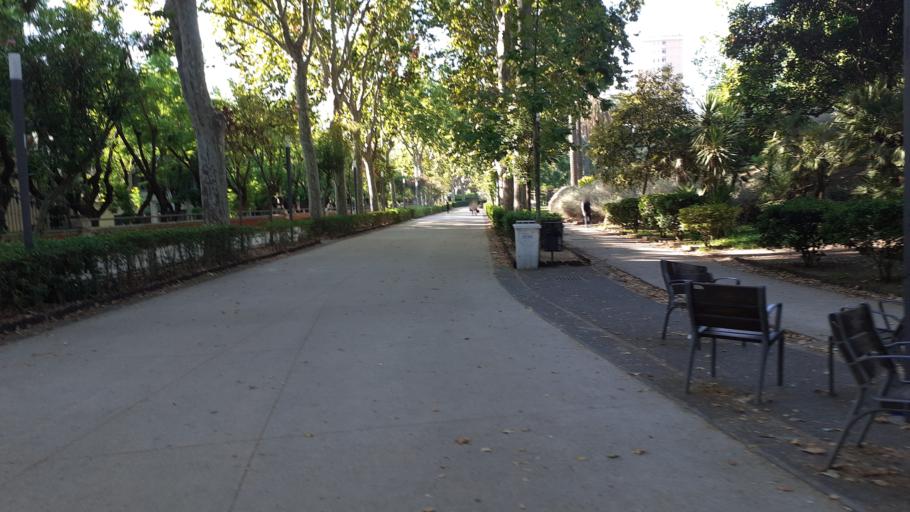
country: IT
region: Sicily
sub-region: Catania
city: Catania
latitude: 37.5126
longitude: 15.0836
